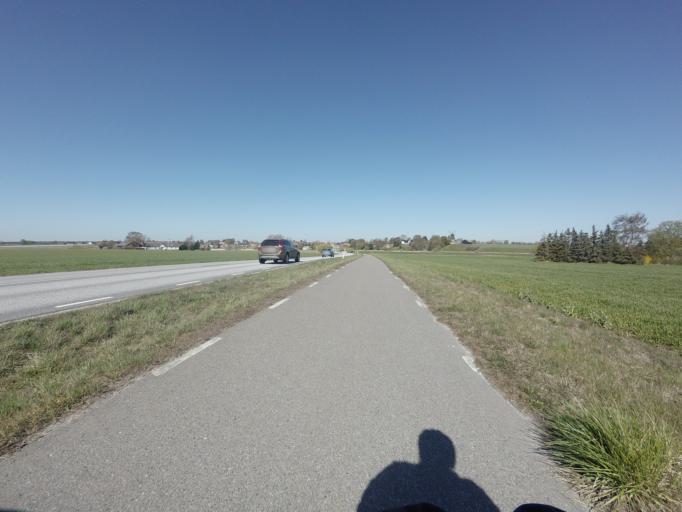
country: SE
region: Skane
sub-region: Kavlinge Kommun
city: Loddekopinge
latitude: 55.7533
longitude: 13.0253
